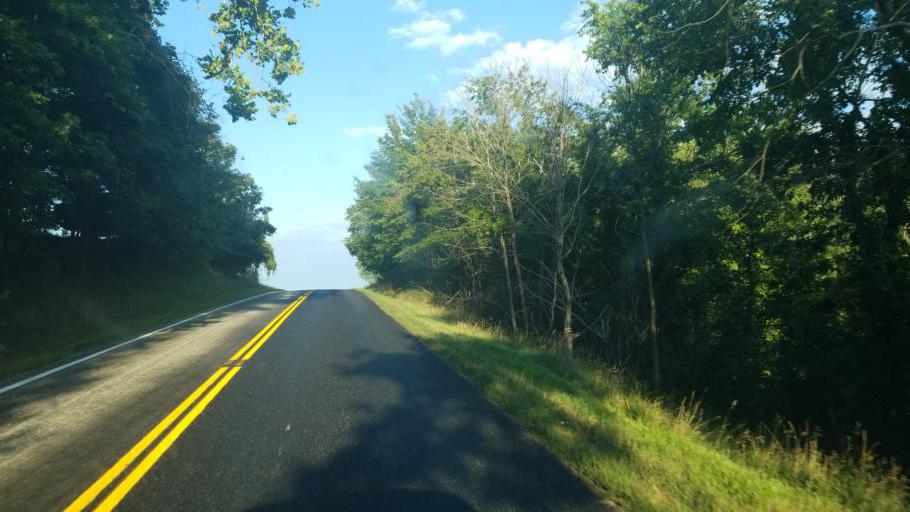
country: US
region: Ohio
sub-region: Huron County
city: Willard
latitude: 41.1054
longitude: -82.7402
